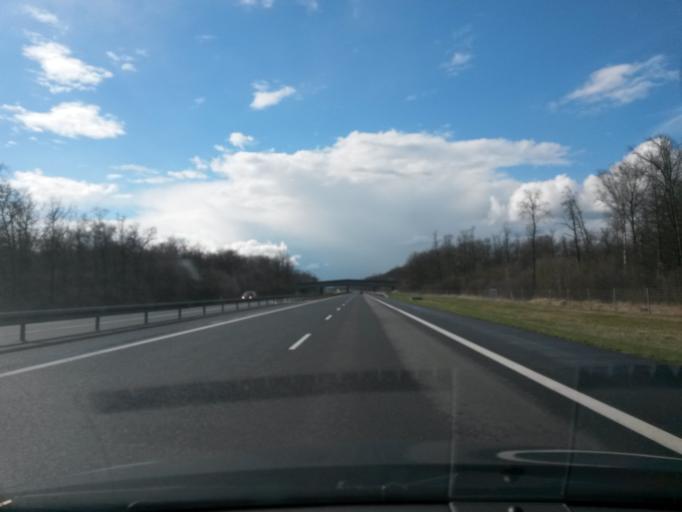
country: PL
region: Greater Poland Voivodeship
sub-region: Powiat wrzesinski
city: Wrzesnia
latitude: 52.3053
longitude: 17.6055
